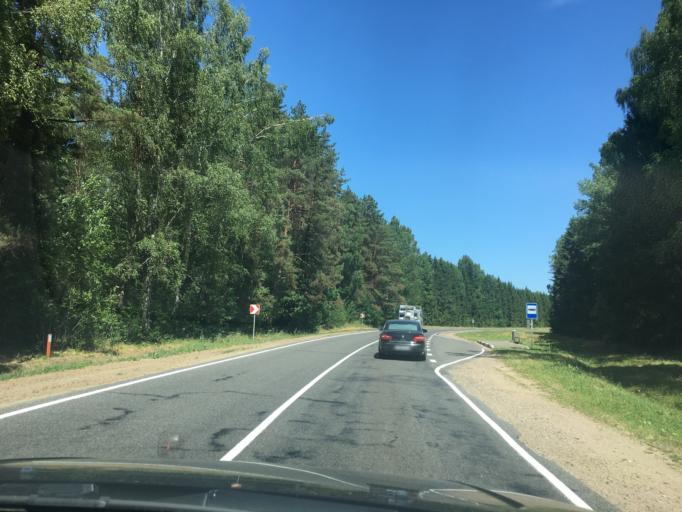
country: BY
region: Grodnenskaya
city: Hal'shany
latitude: 54.1932
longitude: 25.9429
